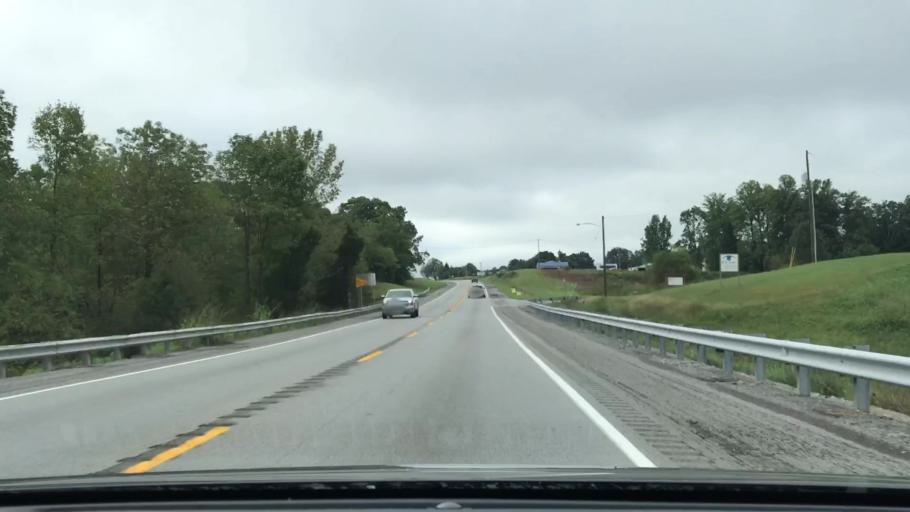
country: US
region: Kentucky
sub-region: Russell County
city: Russell Springs
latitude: 37.0431
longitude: -85.0720
